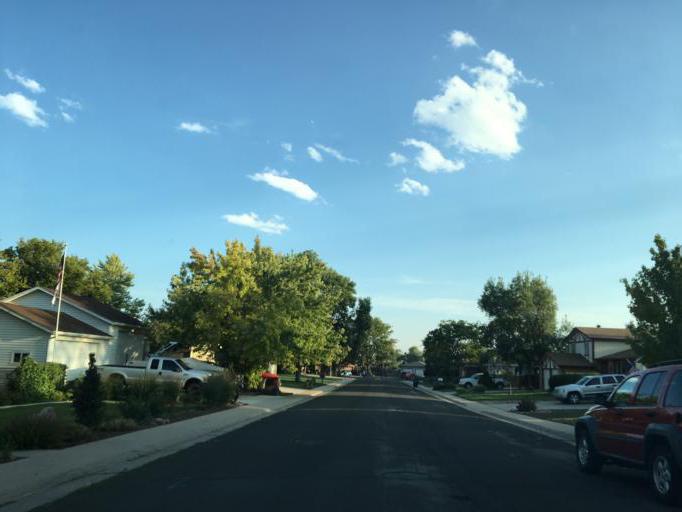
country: US
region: Colorado
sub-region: Jefferson County
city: Applewood
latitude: 39.7908
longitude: -105.1488
